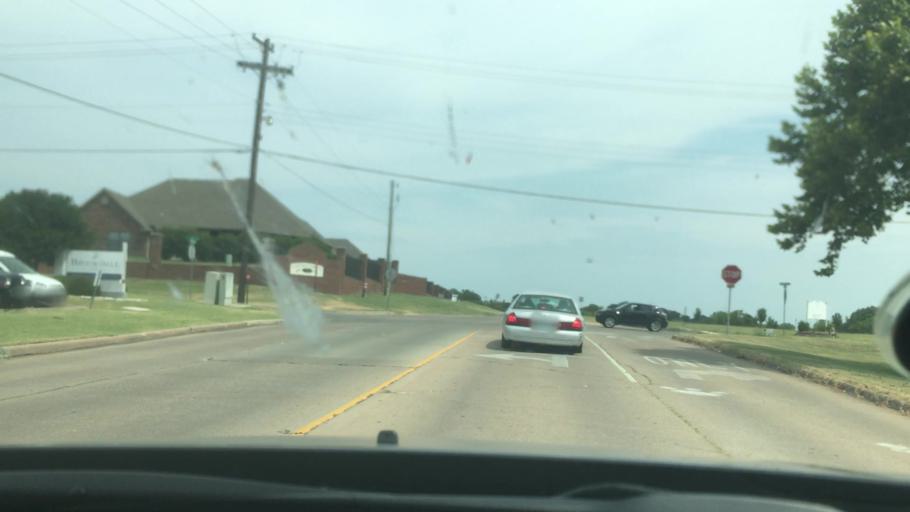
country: US
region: Oklahoma
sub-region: Pontotoc County
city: Ada
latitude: 34.7667
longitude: -96.6611
